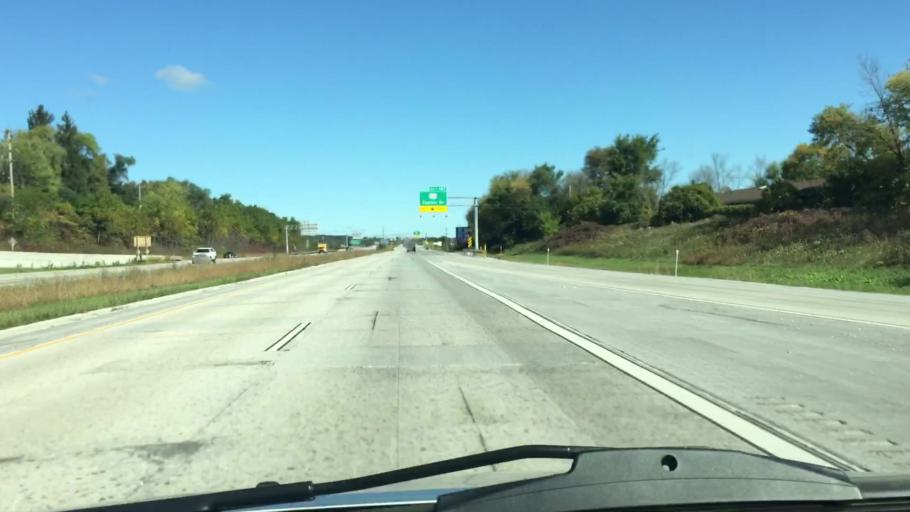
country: US
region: Wisconsin
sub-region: Waukesha County
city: Pewaukee
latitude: 43.0744
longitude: -88.2512
